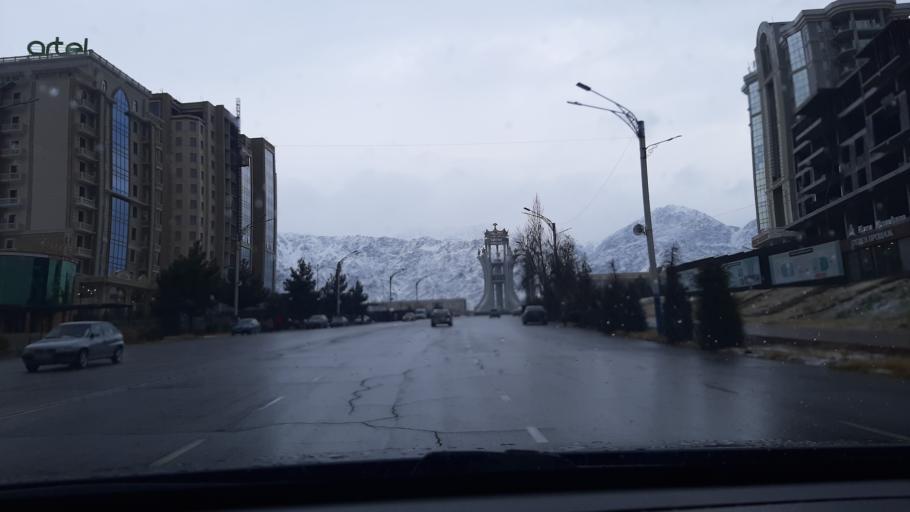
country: TJ
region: Viloyati Sughd
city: Khujand
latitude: 40.2987
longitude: 69.6151
